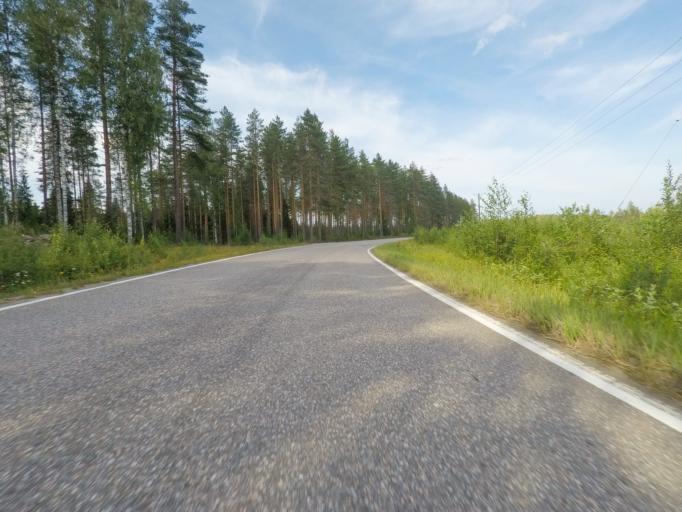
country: FI
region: Southern Savonia
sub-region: Savonlinna
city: Sulkava
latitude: 61.7293
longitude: 28.2066
